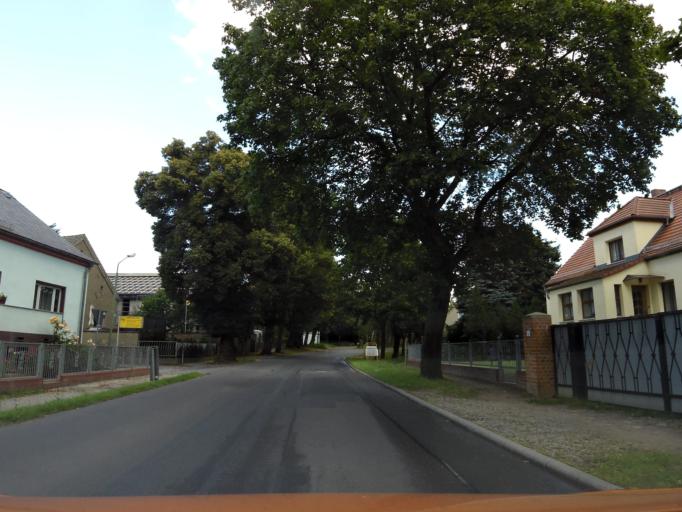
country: DE
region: Brandenburg
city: Potsdam
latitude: 52.4666
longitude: 13.0124
